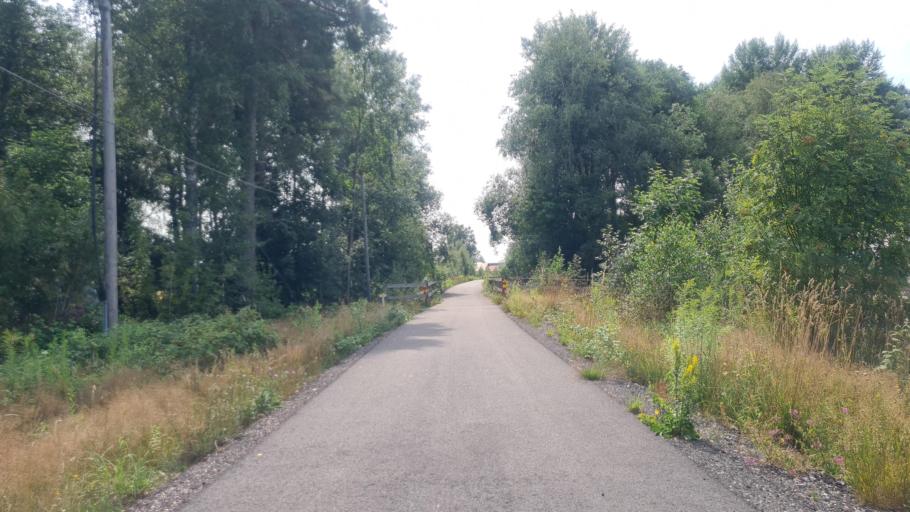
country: SE
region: Kronoberg
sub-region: Ljungby Kommun
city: Lagan
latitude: 56.9070
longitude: 13.9906
